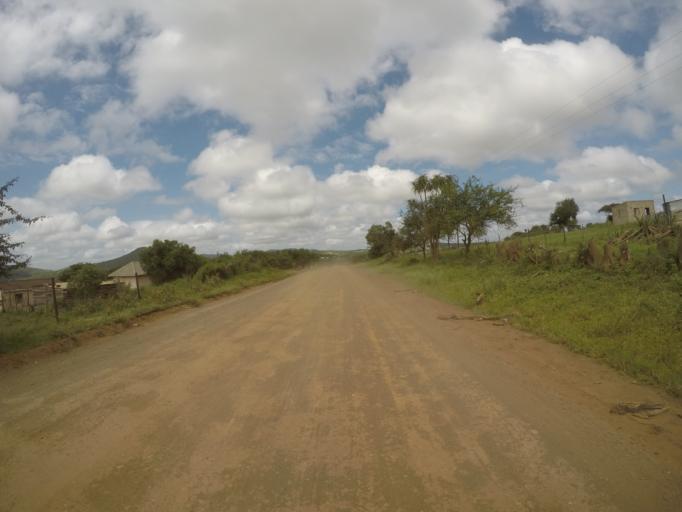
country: ZA
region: KwaZulu-Natal
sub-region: uThungulu District Municipality
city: Empangeni
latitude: -28.5827
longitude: 31.8458
